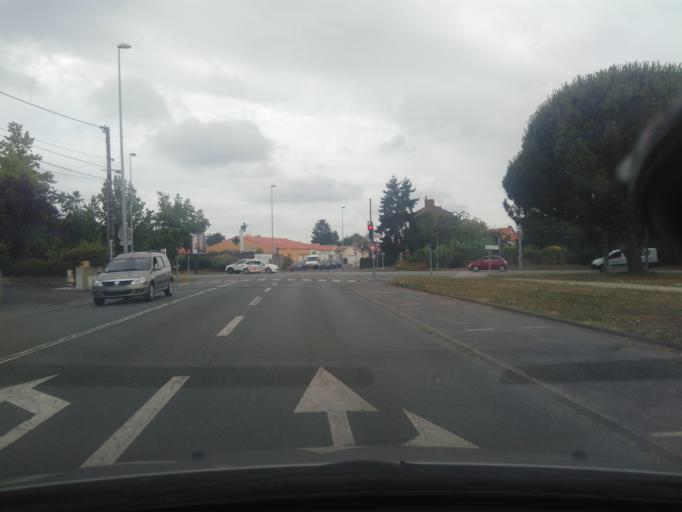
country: FR
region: Pays de la Loire
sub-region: Departement de la Vendee
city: La Roche-sur-Yon
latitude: 46.6640
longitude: -1.4103
